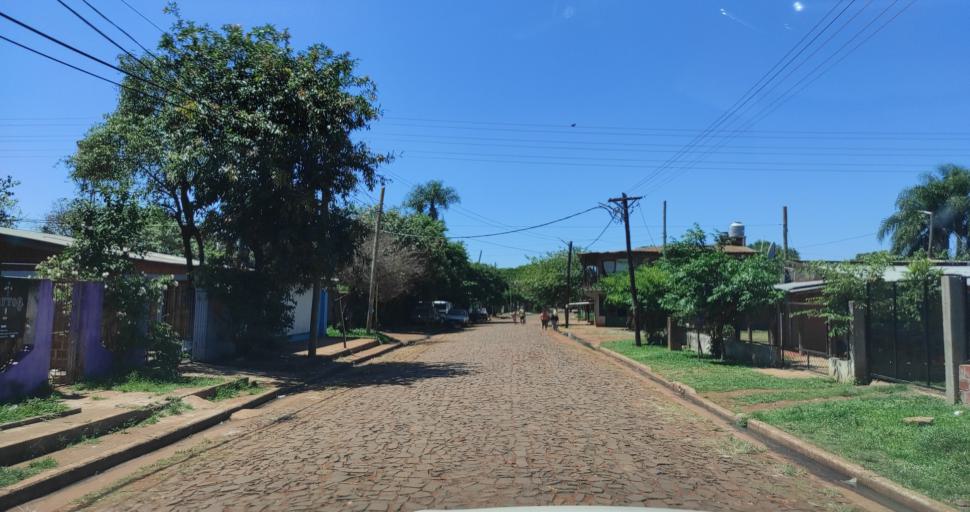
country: AR
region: Misiones
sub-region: Departamento de Capital
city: Posadas
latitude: -27.4139
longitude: -55.9072
